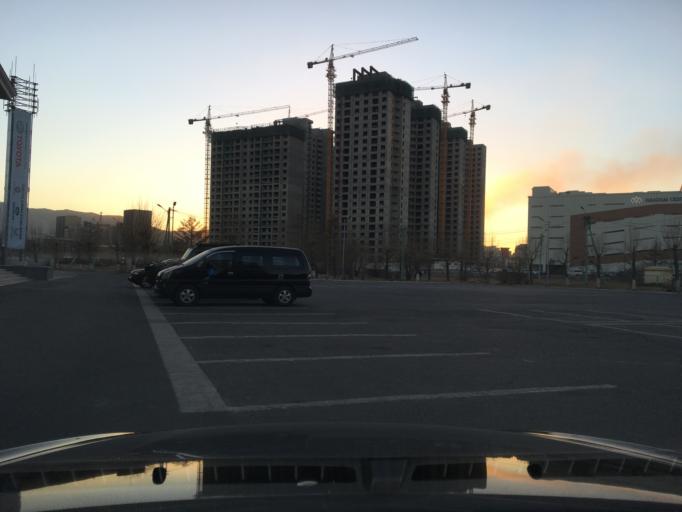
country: MN
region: Ulaanbaatar
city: Ulaanbaatar
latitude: 47.9029
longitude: 106.9158
